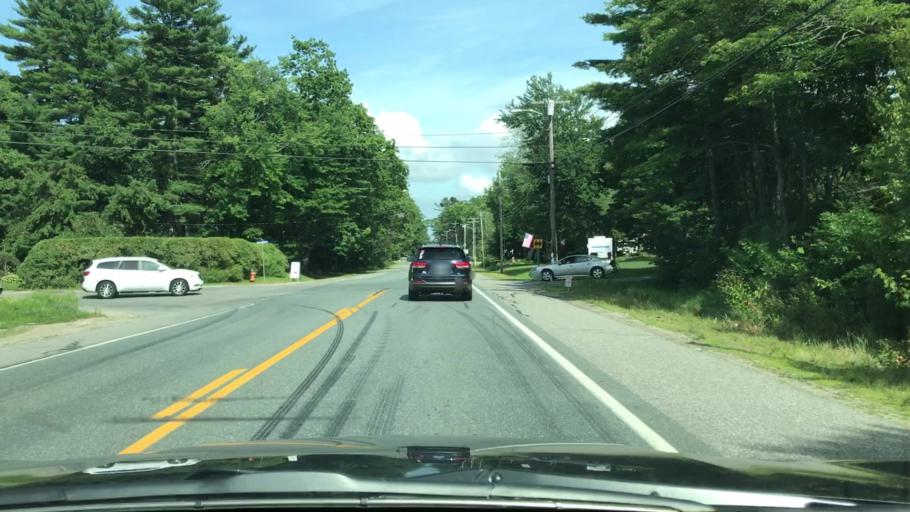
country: US
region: Maine
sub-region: Hancock County
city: Ellsworth
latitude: 44.5392
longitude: -68.4407
